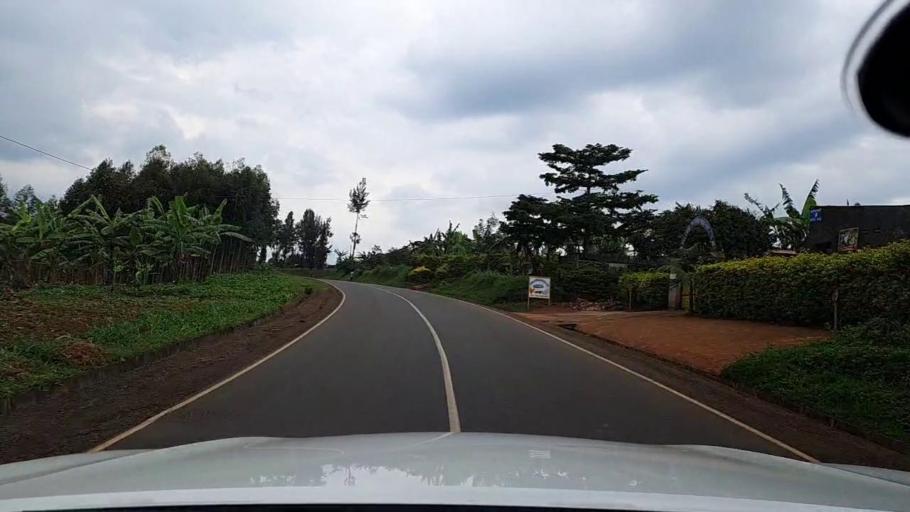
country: RW
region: Western Province
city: Cyangugu
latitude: -2.5930
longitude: 28.9248
